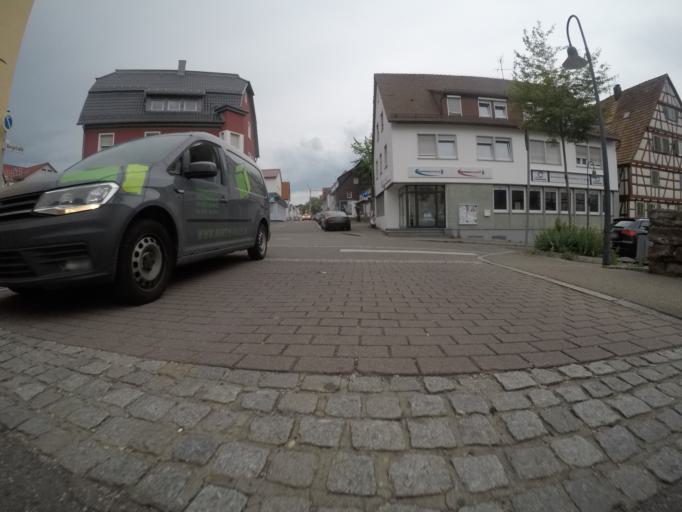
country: DE
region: Baden-Wuerttemberg
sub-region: Regierungsbezirk Stuttgart
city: Leonberg
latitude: 48.7895
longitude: 9.0075
